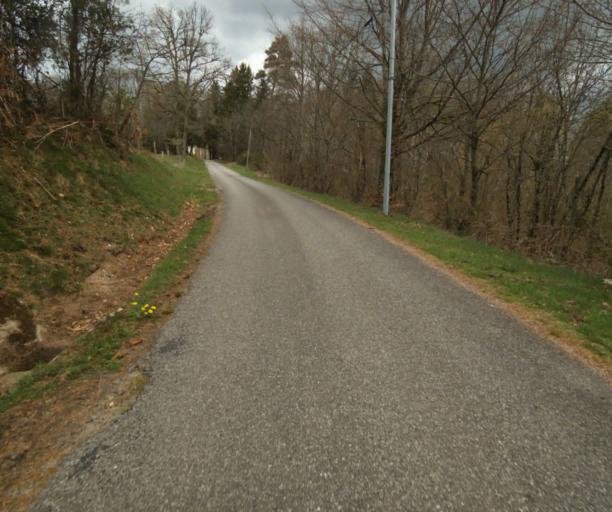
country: FR
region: Limousin
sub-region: Departement de la Correze
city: Laguenne
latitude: 45.2376
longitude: 1.8979
